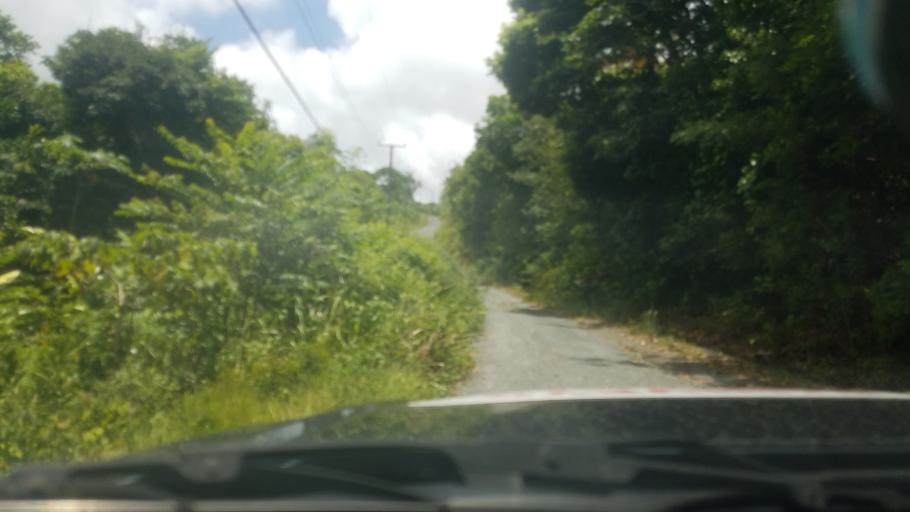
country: LC
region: Praslin
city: Praslin
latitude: 13.8671
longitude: -60.9121
